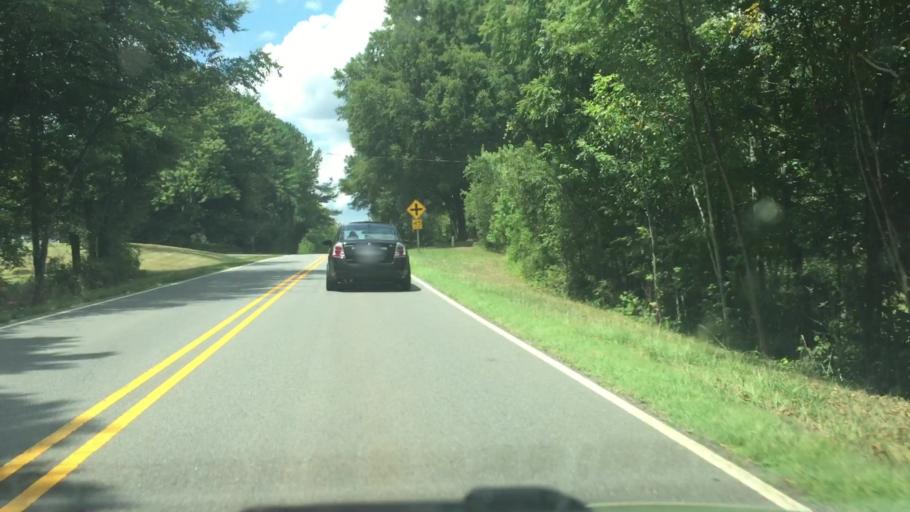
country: US
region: North Carolina
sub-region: Rowan County
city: Enochville
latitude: 35.4884
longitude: -80.6853
